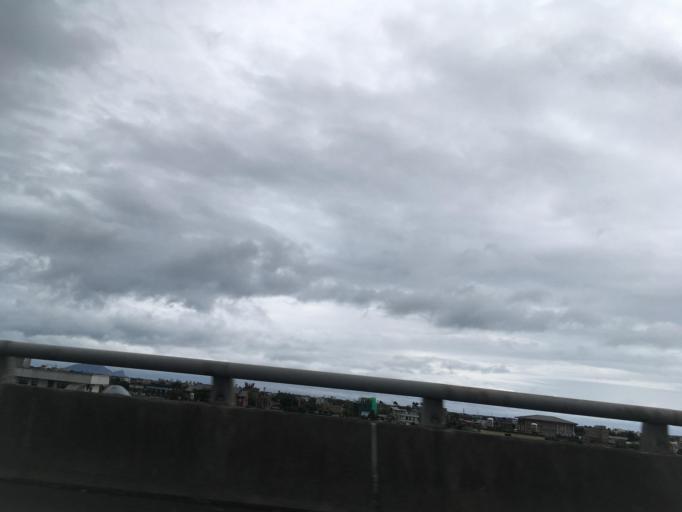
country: TW
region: Taiwan
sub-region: Yilan
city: Yilan
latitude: 24.7977
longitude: 121.7824
